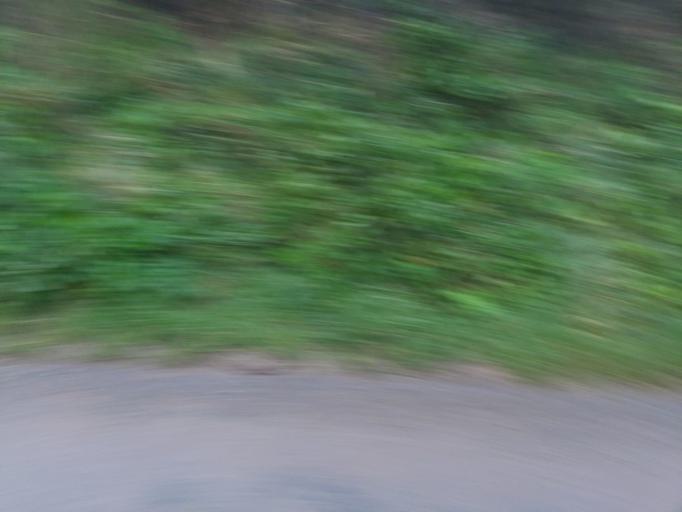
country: GB
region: England
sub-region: Cornwall
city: Torpoint
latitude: 50.3336
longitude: -4.2207
